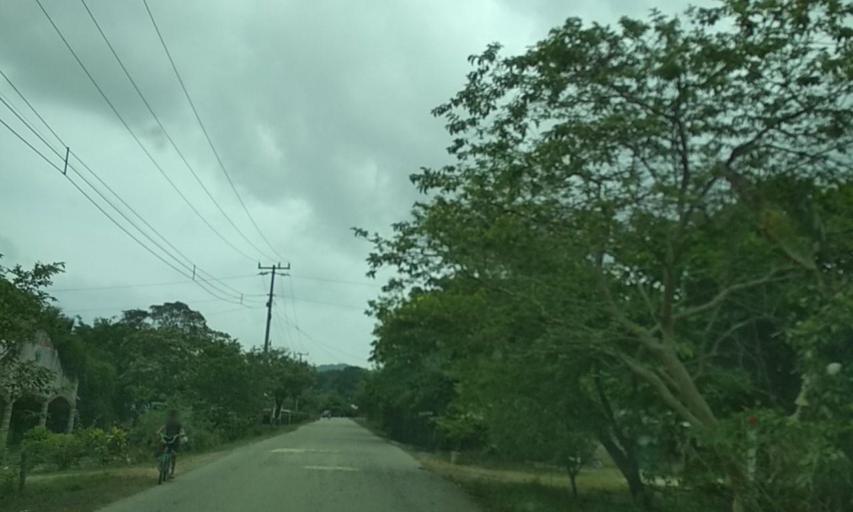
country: MX
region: Veracruz
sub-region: Uxpanapa
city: Poblado 10
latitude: 17.4723
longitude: -94.1210
